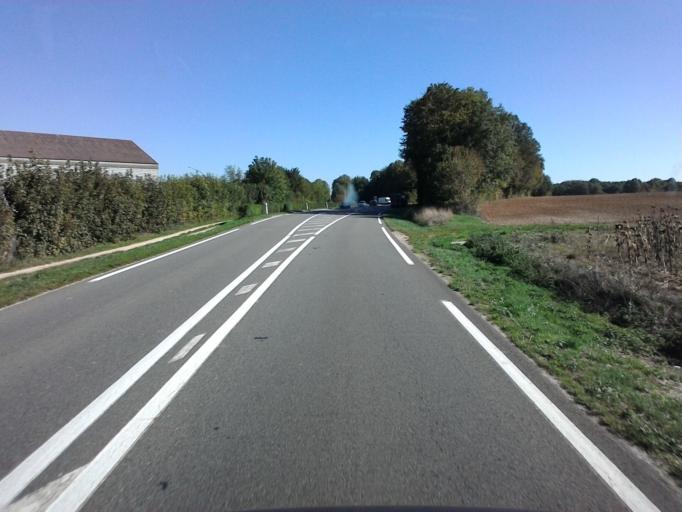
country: FR
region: Champagne-Ardenne
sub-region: Departement de la Haute-Marne
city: Chaumont
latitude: 48.1119
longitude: 5.0885
